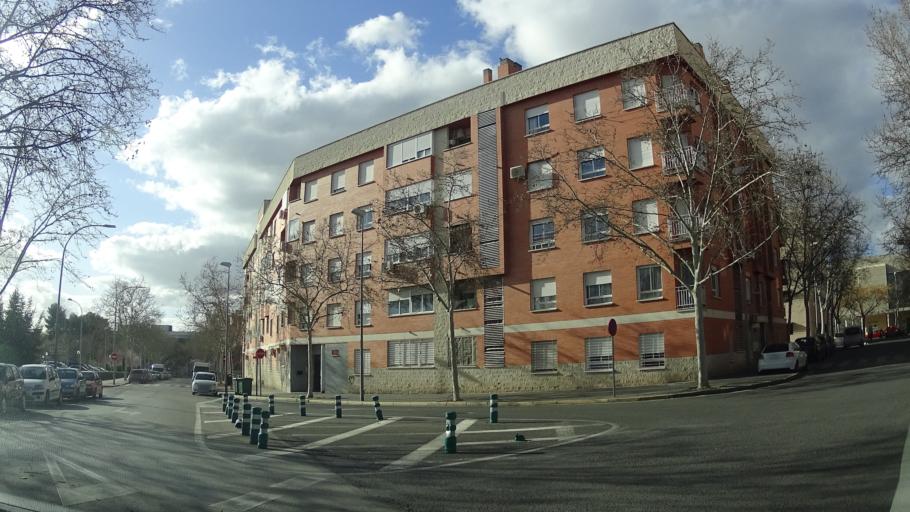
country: ES
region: Castille-La Mancha
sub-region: Provincia de Ciudad Real
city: Ciudad Real
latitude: 38.9782
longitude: -3.9335
